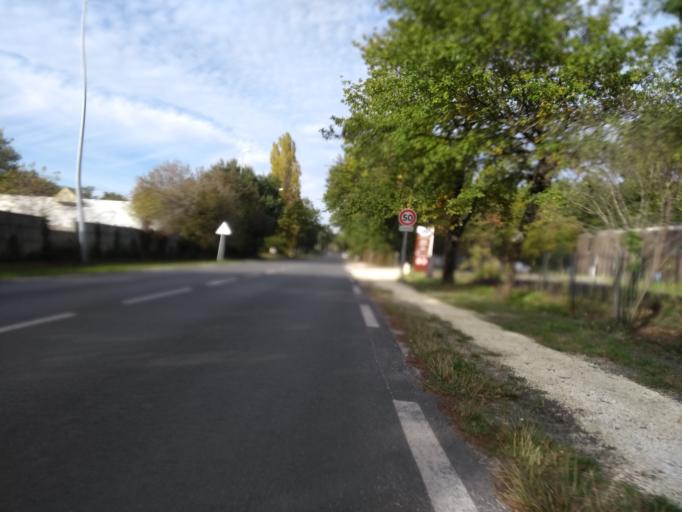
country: FR
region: Aquitaine
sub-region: Departement de la Gironde
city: Canejan
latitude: 44.7788
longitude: -0.6629
